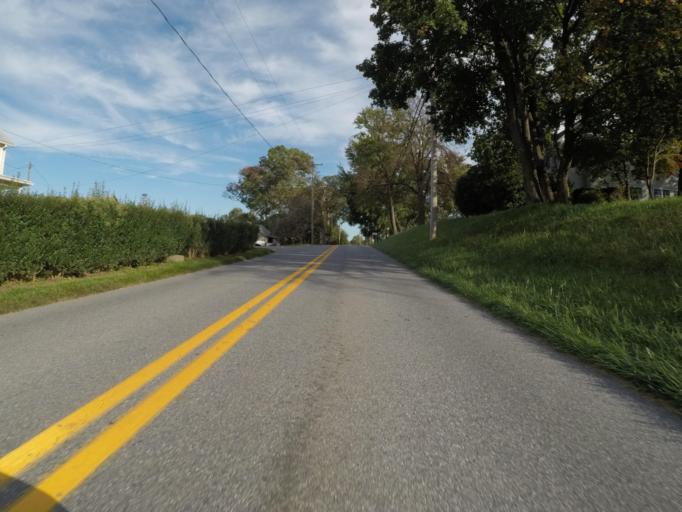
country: US
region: Maryland
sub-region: Carroll County
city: Hampstead
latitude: 39.5438
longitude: -76.7971
